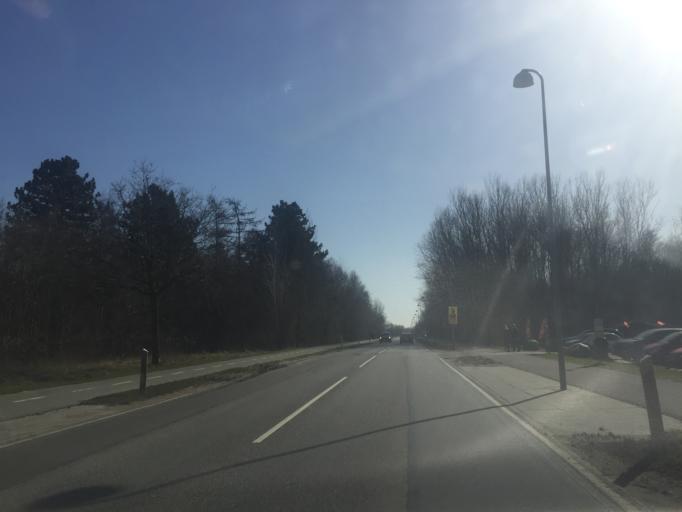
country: DK
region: Capital Region
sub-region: Glostrup Kommune
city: Glostrup
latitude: 55.6875
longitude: 12.4215
